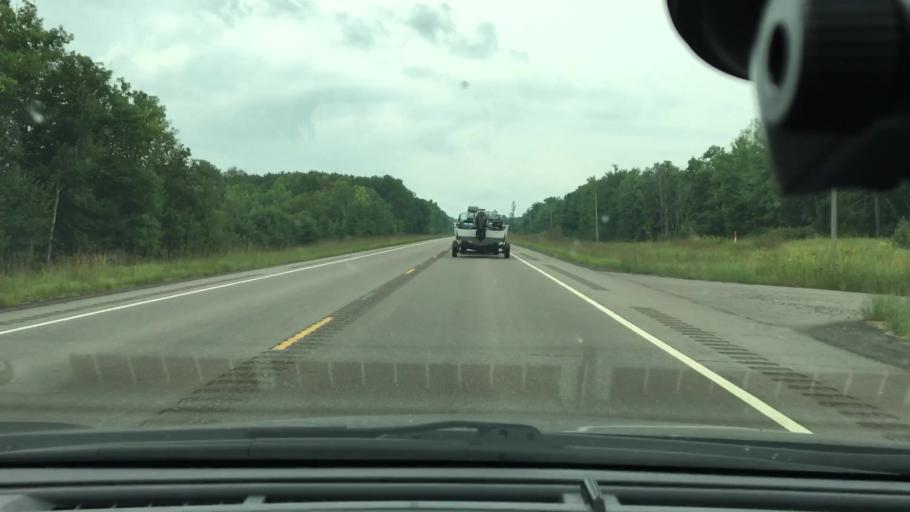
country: US
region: Minnesota
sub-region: Crow Wing County
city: Crosby
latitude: 46.5859
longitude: -93.9527
